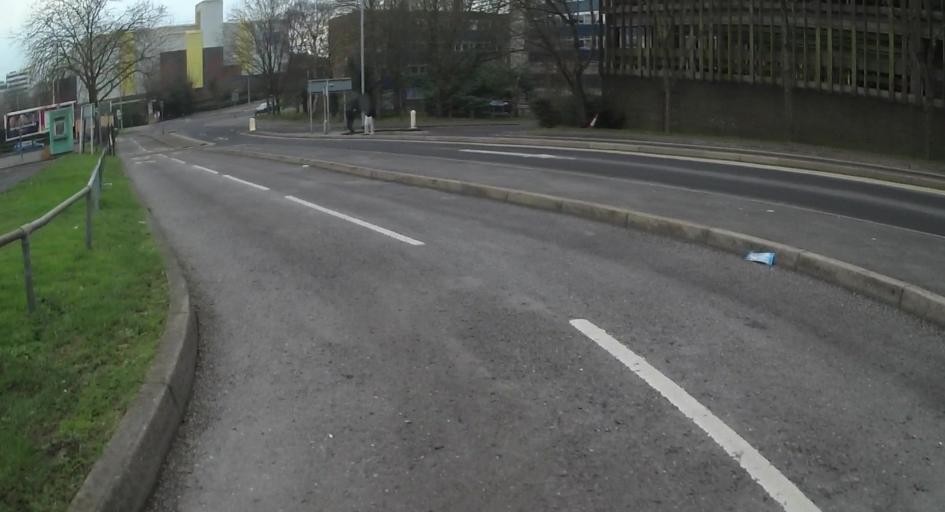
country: GB
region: England
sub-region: Bracknell Forest
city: Bracknell
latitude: 51.4174
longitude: -0.7537
